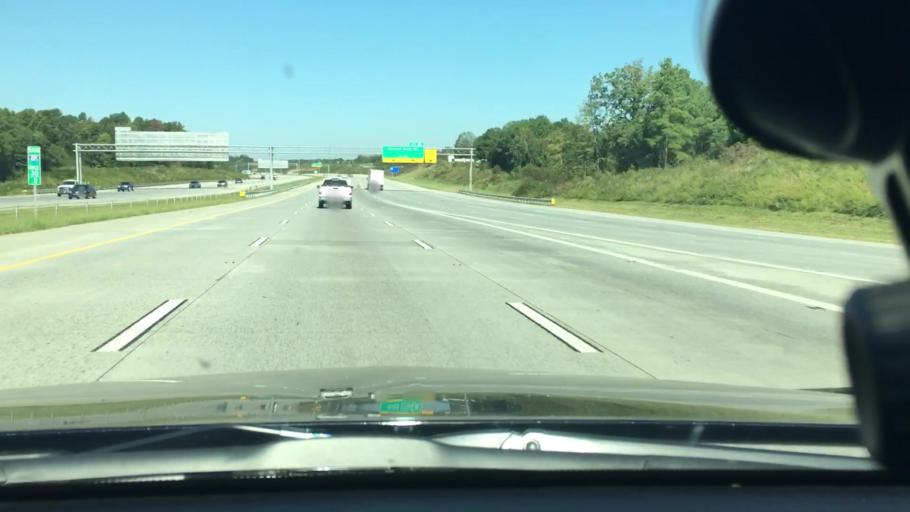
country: US
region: North Carolina
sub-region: Cabarrus County
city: Harrisburg
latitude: 35.3541
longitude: -80.7381
